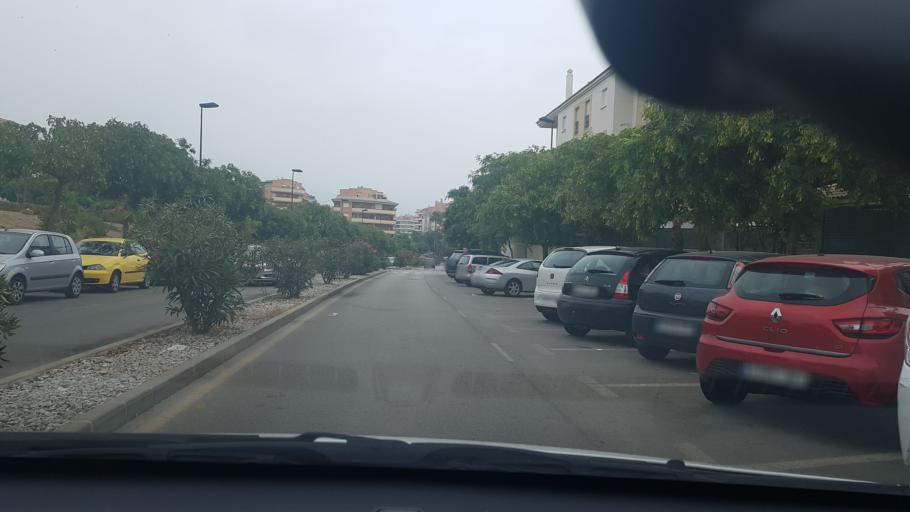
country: ES
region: Andalusia
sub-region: Provincia de Malaga
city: Manilva
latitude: 36.3624
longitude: -5.2311
